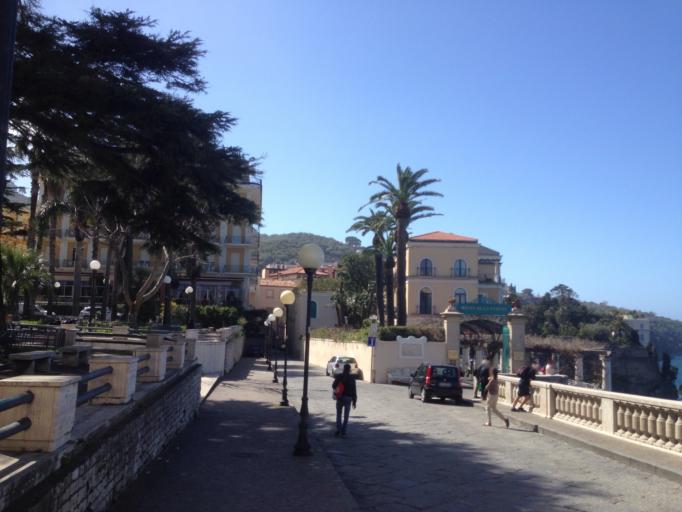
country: IT
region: Campania
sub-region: Provincia di Napoli
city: Sorrento
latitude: 40.6275
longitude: 14.3714
